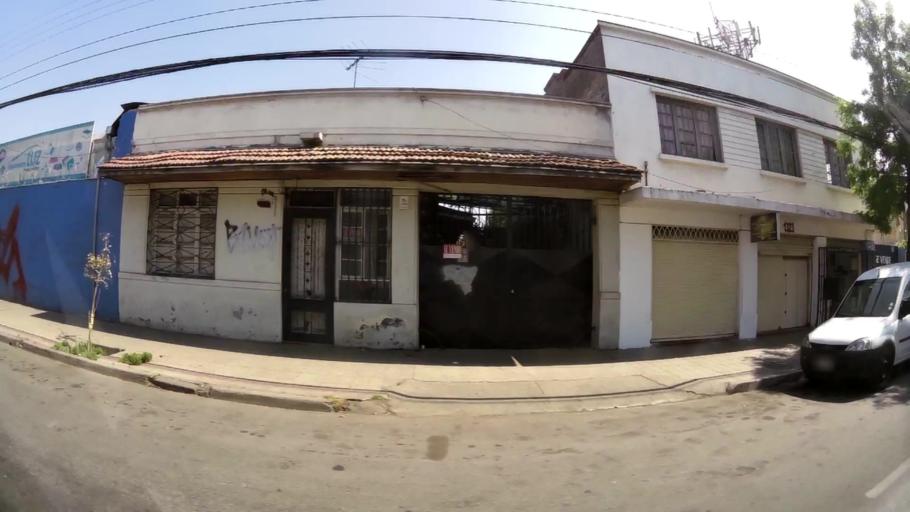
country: CL
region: Santiago Metropolitan
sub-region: Provincia de Santiago
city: Santiago
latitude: -33.4655
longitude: -70.6733
